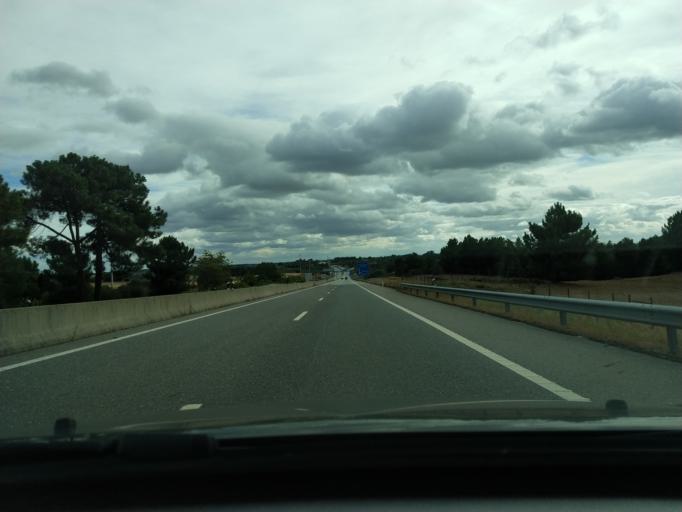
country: PT
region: Castelo Branco
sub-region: Concelho do Fundao
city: Fundao
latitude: 40.0402
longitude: -7.4698
